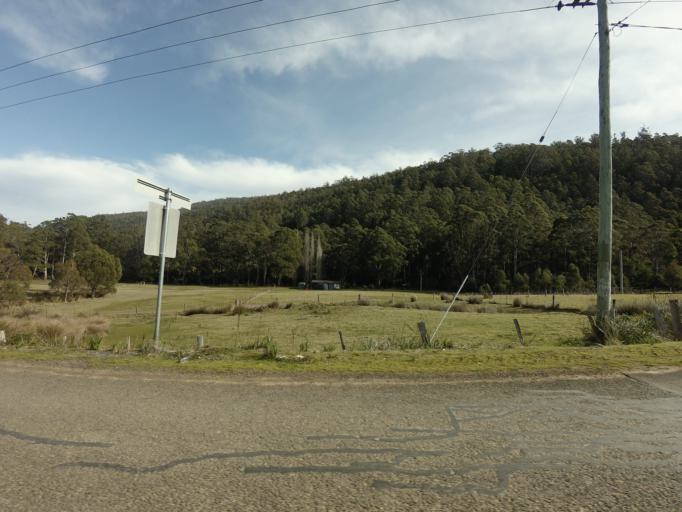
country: AU
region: Tasmania
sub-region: Huon Valley
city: Huonville
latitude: -43.0514
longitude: 147.1071
